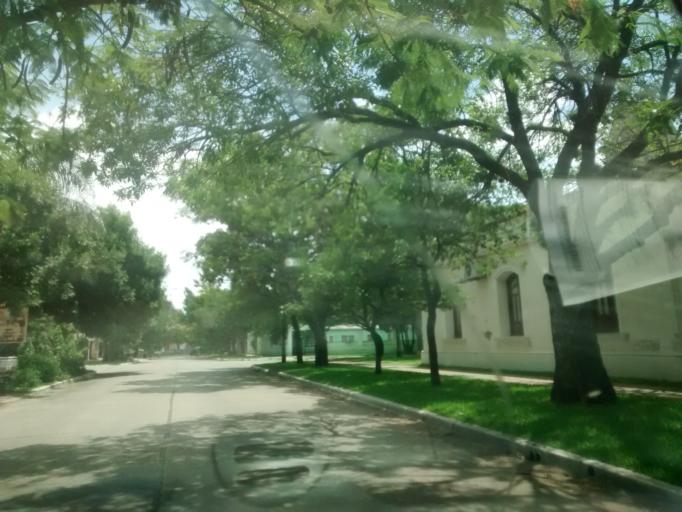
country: AR
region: Chaco
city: Resistencia
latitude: -27.4405
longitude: -58.9869
